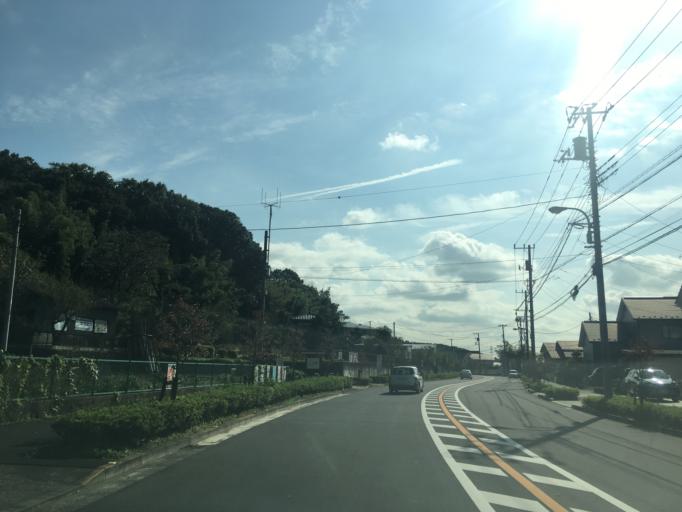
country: JP
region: Tokyo
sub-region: Machida-shi
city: Machida
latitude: 35.5932
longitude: 139.4150
